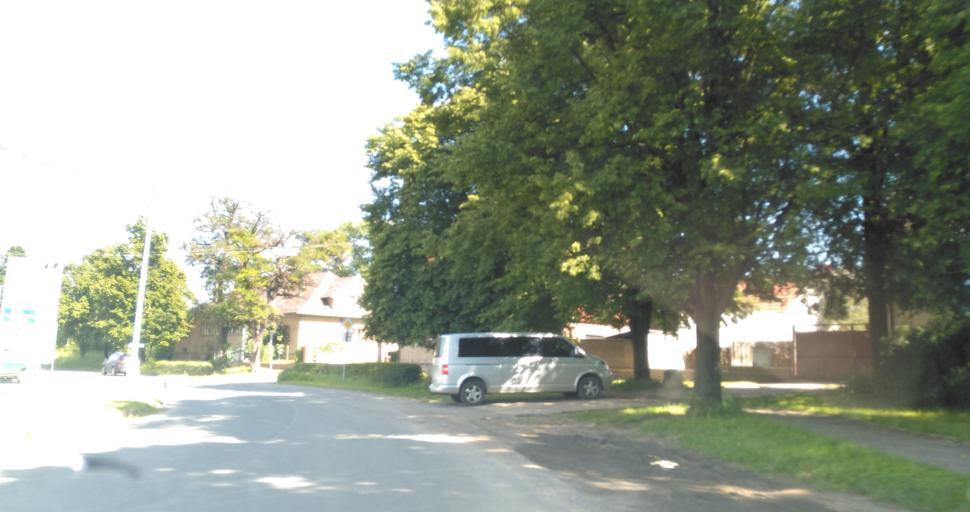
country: CZ
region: Central Bohemia
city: Revnice
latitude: 49.9028
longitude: 14.1533
